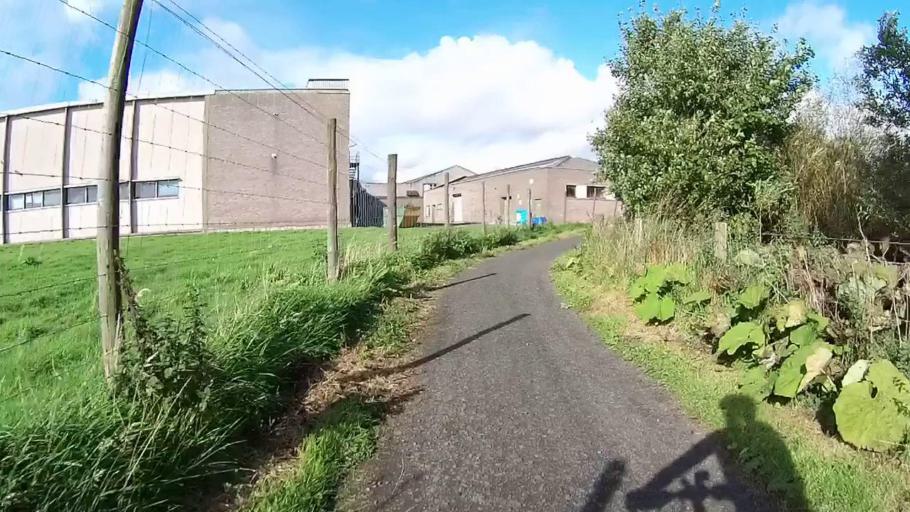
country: GB
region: Scotland
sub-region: Perth and Kinross
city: Kinross
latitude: 56.1968
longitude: -3.4199
